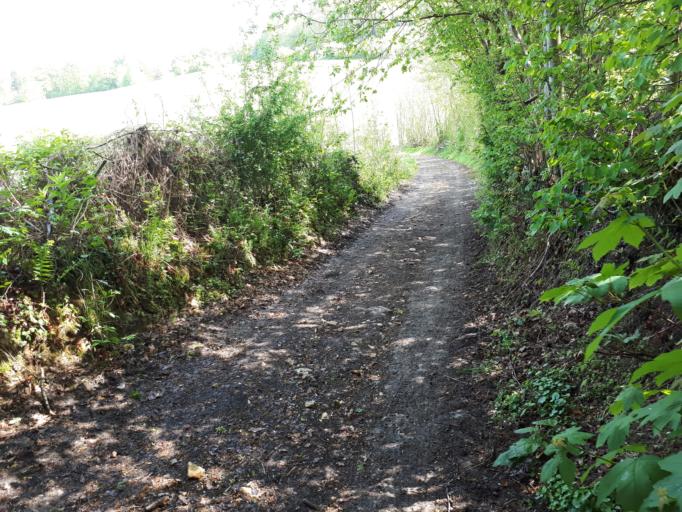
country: BE
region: Wallonia
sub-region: Province de Liege
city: Plombieres
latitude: 50.7594
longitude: 5.9840
